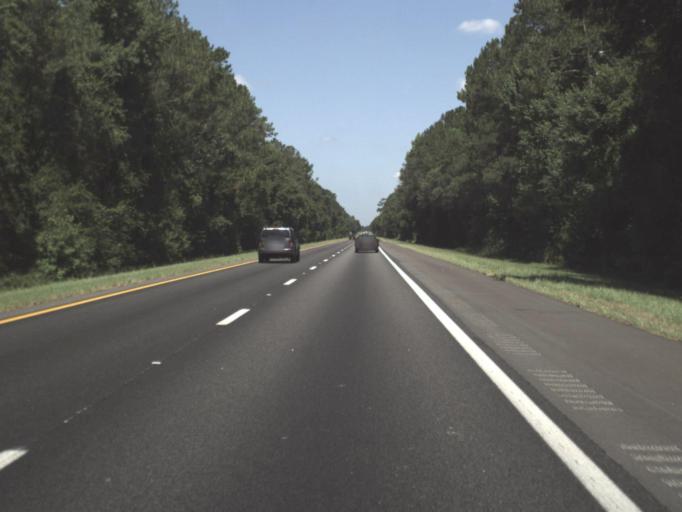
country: US
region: Florida
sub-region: Madison County
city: Madison
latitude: 30.4068
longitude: -83.4036
